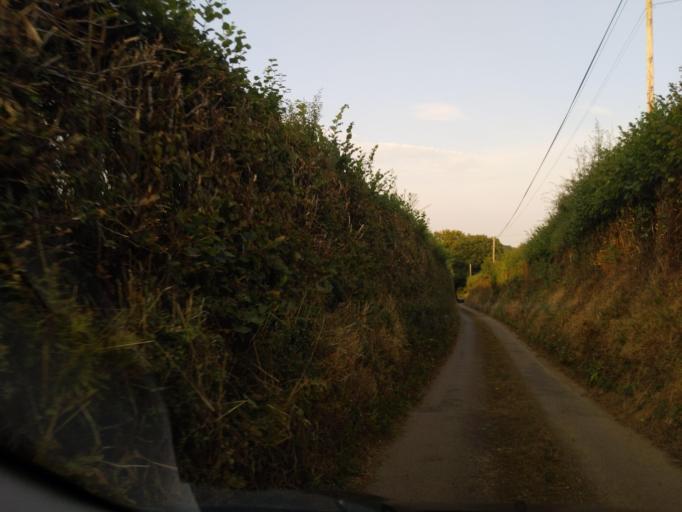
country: GB
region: England
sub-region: Cornwall
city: Fowey
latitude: 50.3678
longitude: -4.5769
